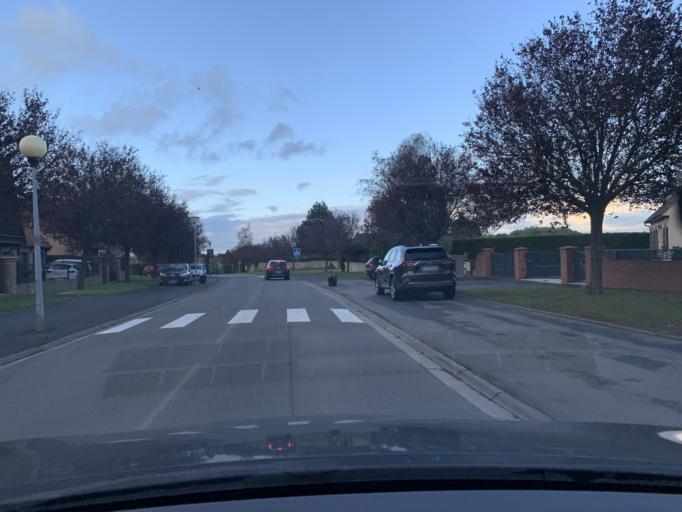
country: FR
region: Nord-Pas-de-Calais
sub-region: Departement du Nord
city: Proville
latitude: 50.1554
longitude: 3.2110
